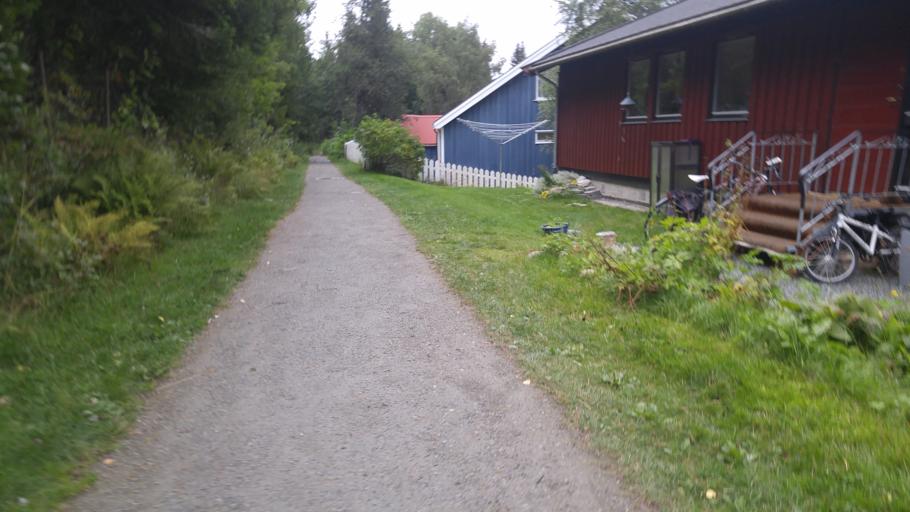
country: NO
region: Sor-Trondelag
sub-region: Trondheim
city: Trondheim
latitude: 63.4057
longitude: 10.3190
